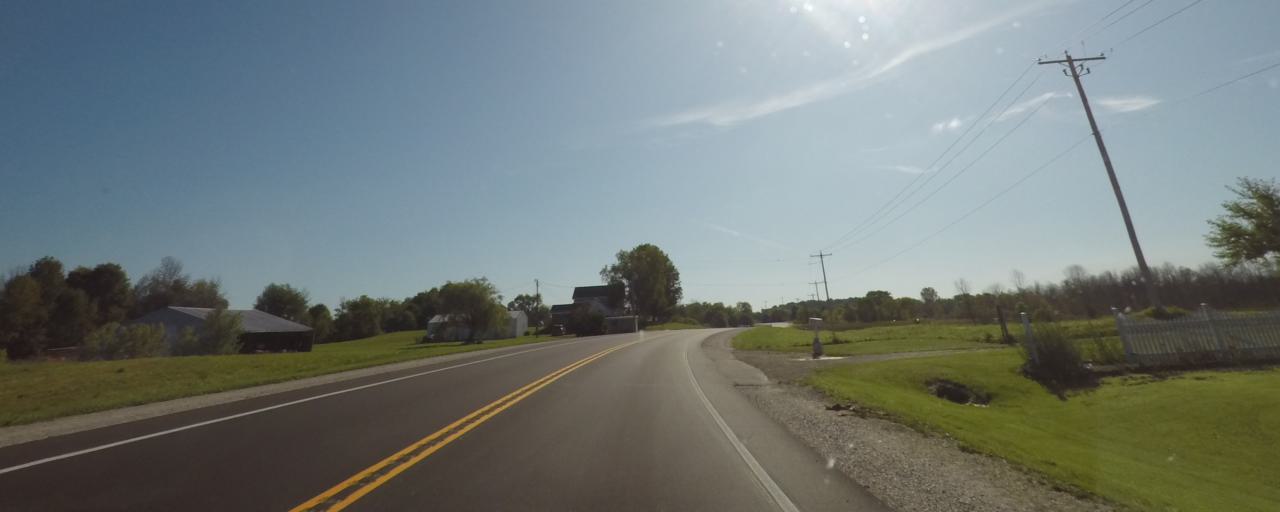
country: US
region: Wisconsin
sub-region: Jefferson County
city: Johnson Creek
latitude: 43.0142
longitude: -88.6751
